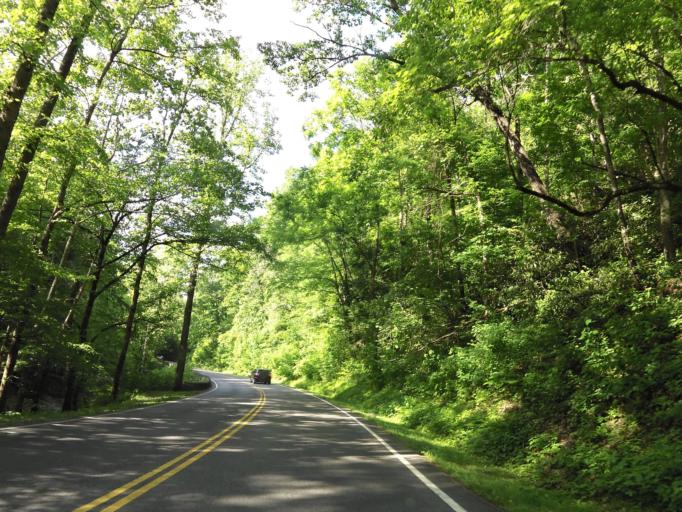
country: US
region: Tennessee
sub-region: Sevier County
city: Gatlinburg
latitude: 35.6981
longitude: -83.5271
